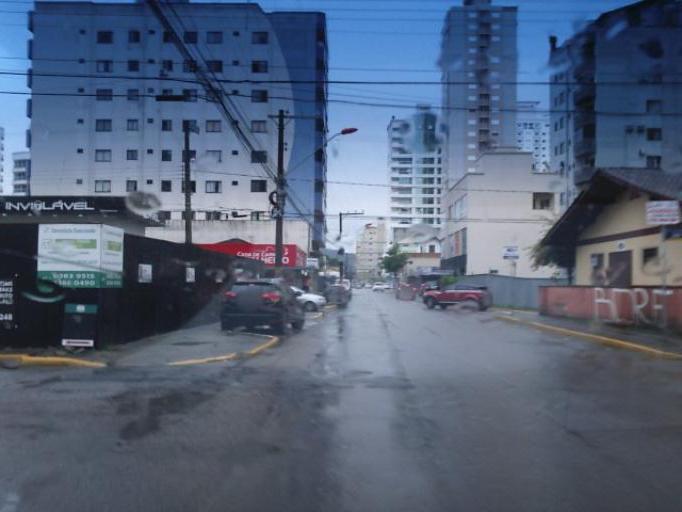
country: BR
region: Santa Catarina
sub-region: Itapema
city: Itapema
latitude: -27.1289
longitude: -48.6050
